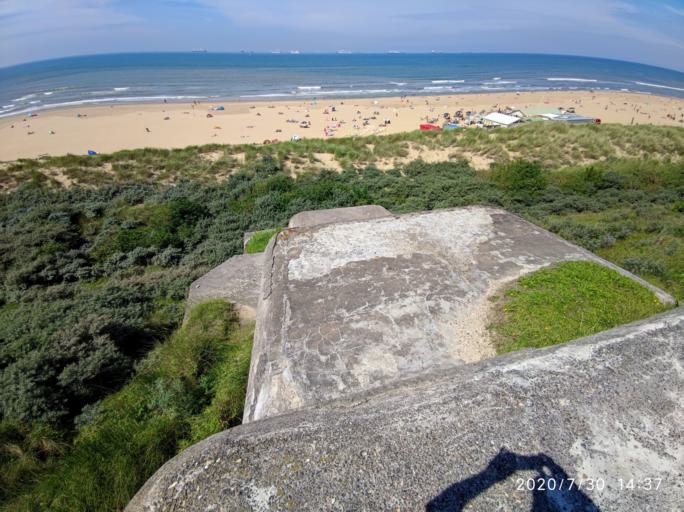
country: NL
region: South Holland
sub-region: Gemeente Den Haag
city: Scheveningen
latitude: 52.1250
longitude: 4.3002
